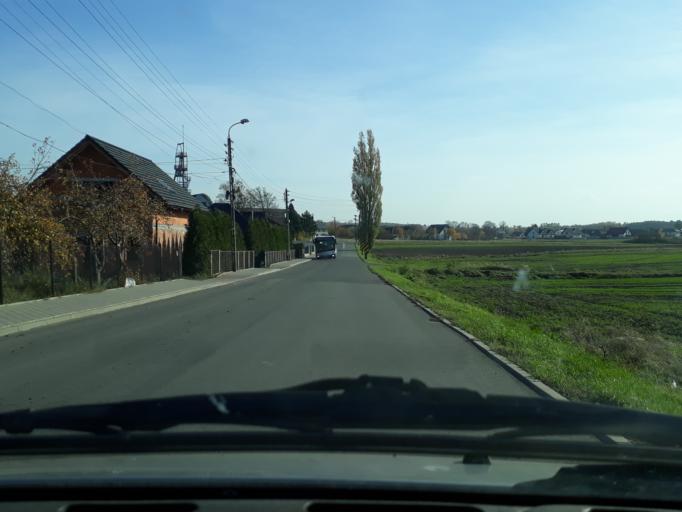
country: PL
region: Silesian Voivodeship
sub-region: Powiat tarnogorski
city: Tarnowskie Gory
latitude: 50.4266
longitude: 18.8467
